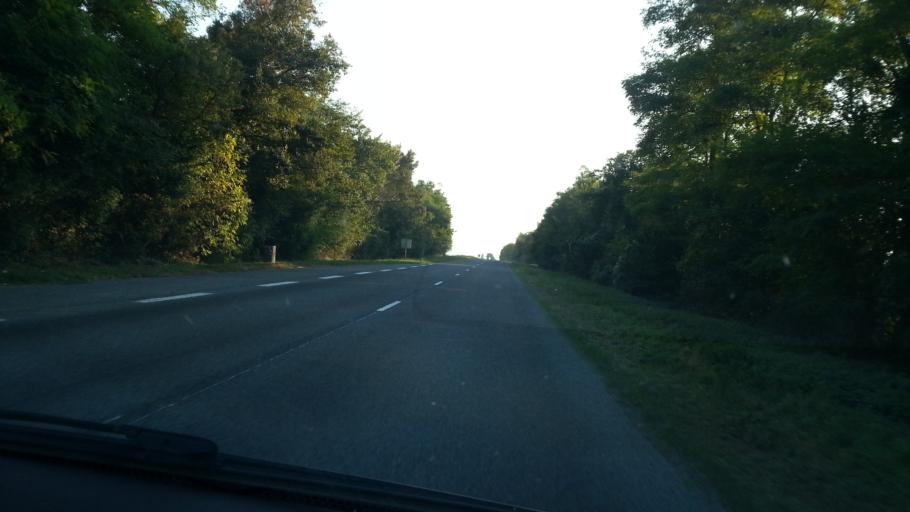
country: FR
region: Picardie
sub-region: Departement de l'Oise
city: Grandfresnoy
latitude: 49.3765
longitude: 2.6176
